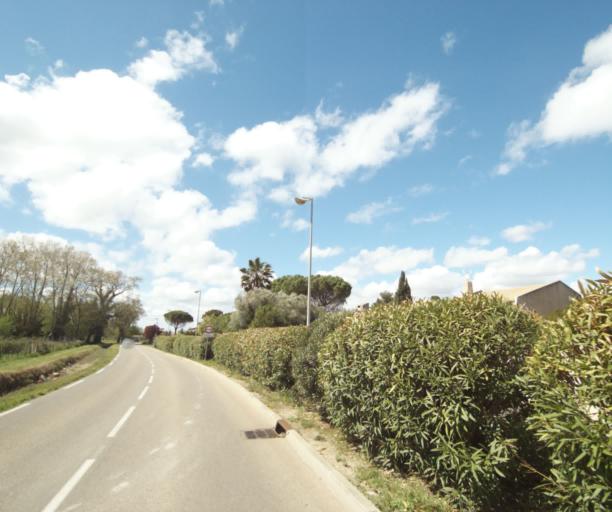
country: FR
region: Languedoc-Roussillon
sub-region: Departement de l'Herault
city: Lattes
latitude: 43.5655
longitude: 3.9153
